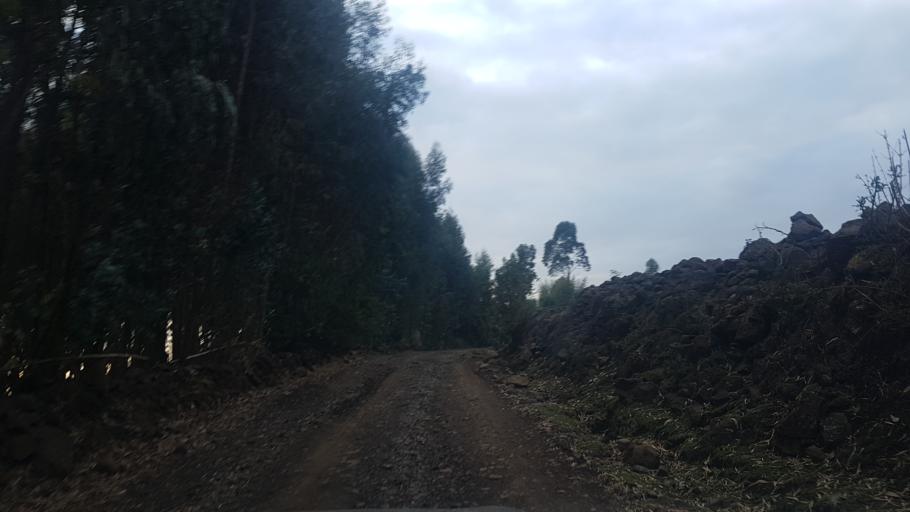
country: ET
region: Amhara
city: Finote Selam
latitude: 10.8042
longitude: 37.6607
